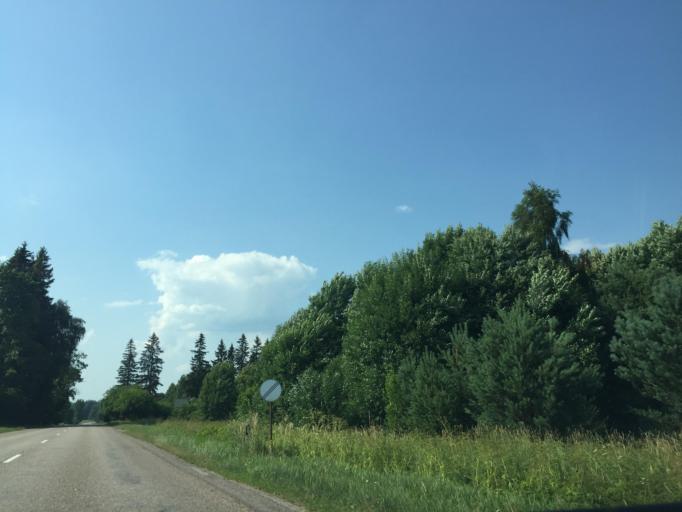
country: LV
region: Limbazu Rajons
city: Limbazi
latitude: 57.5008
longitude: 24.8360
